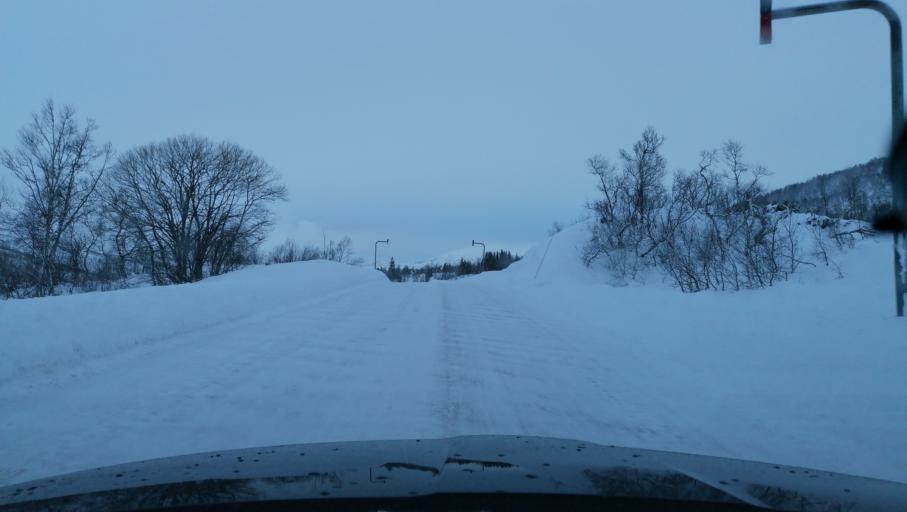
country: NO
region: Aust-Agder
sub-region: Bykle
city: Hovden
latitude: 59.6358
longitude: 7.4539
